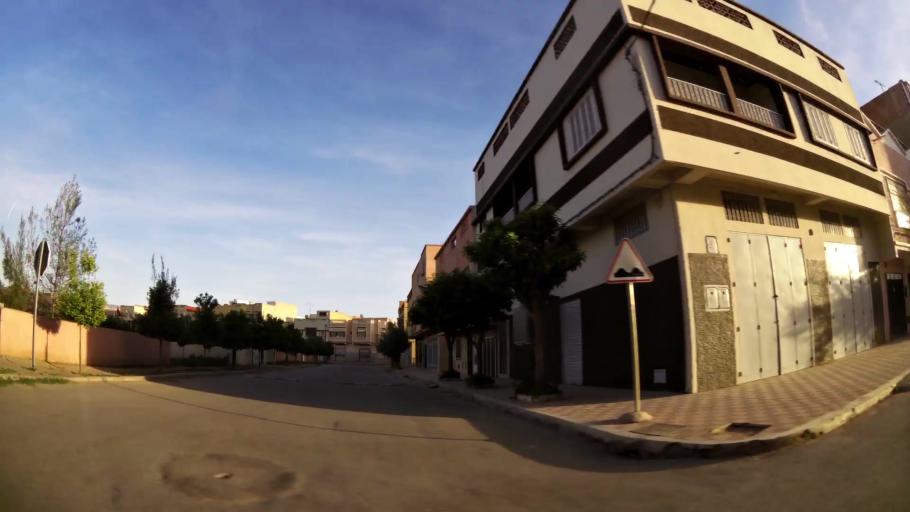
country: MA
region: Oriental
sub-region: Oujda-Angad
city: Oujda
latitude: 34.6774
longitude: -1.8957
